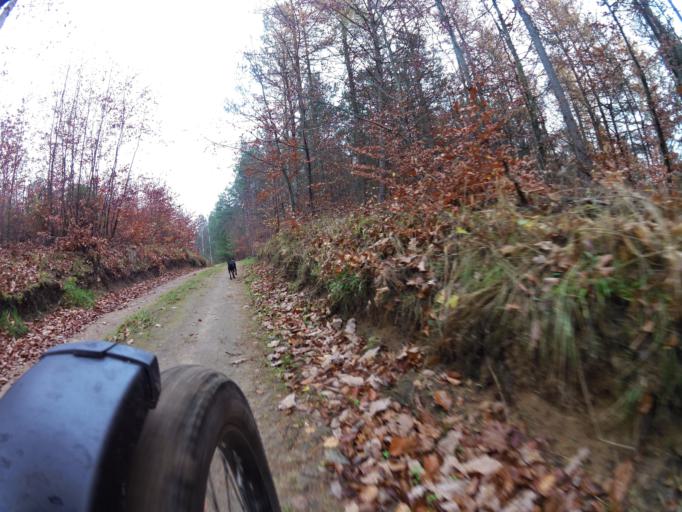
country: PL
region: Pomeranian Voivodeship
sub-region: Powiat wejherowski
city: Orle
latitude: 54.6994
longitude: 18.1551
